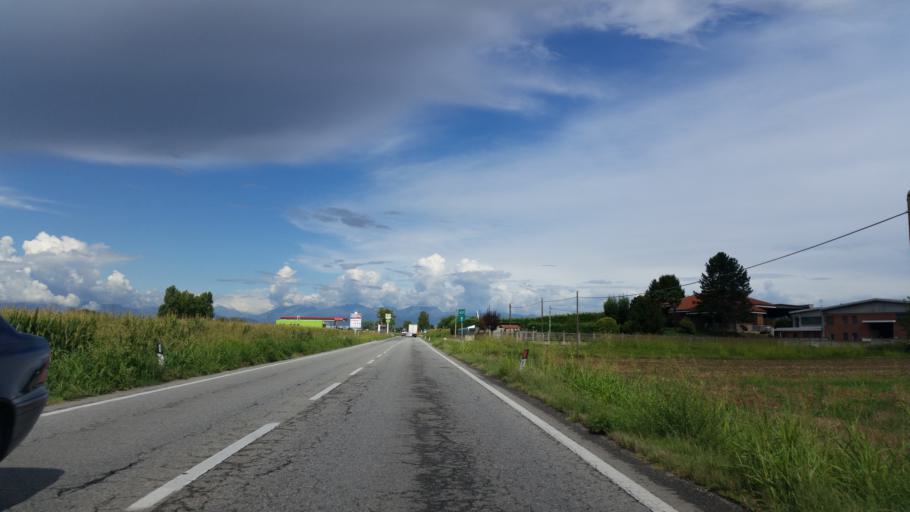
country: IT
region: Piedmont
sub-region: Provincia di Torino
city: Marocchi
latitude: 44.9457
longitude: 7.8096
